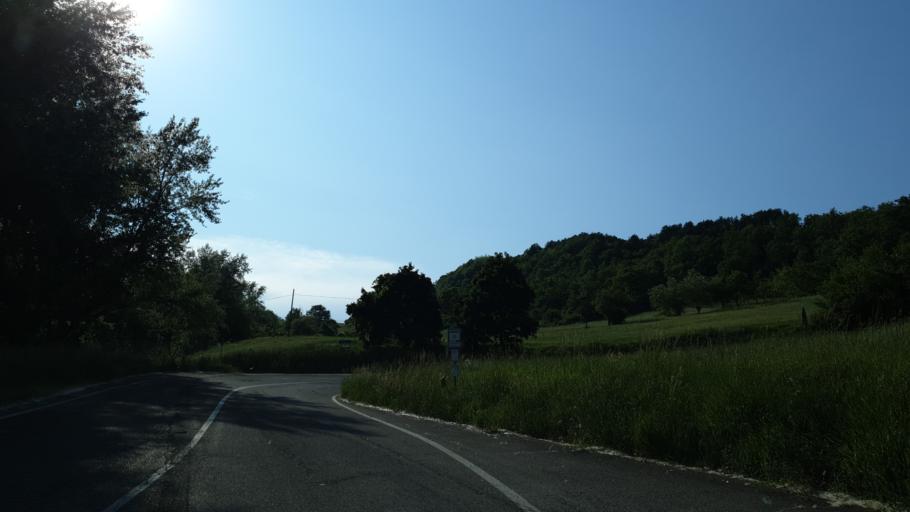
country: IT
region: Tuscany
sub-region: Province of Arezzo
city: Stia
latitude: 43.7721
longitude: 11.6938
